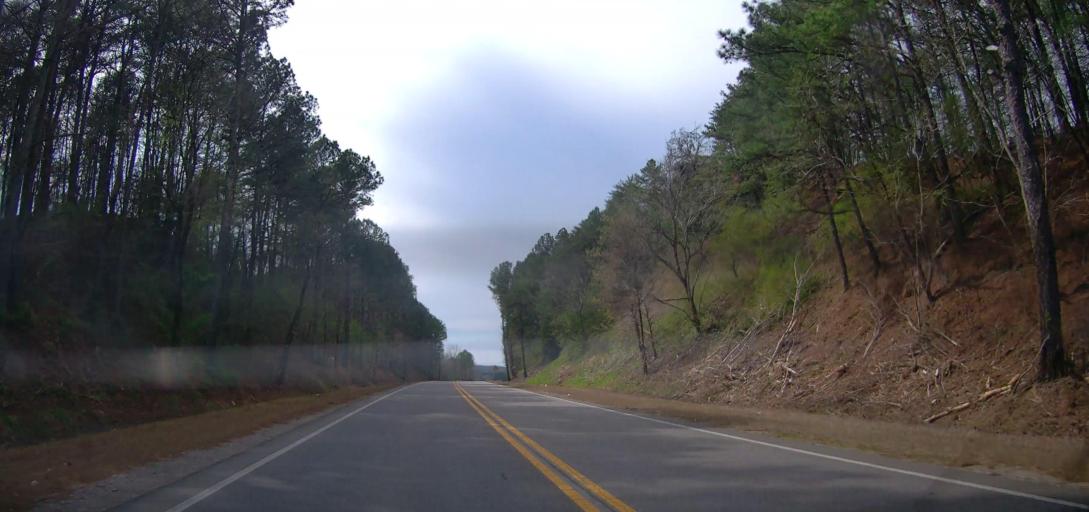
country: US
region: Alabama
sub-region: Walker County
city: Carbon Hill
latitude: 33.8763
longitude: -87.4877
